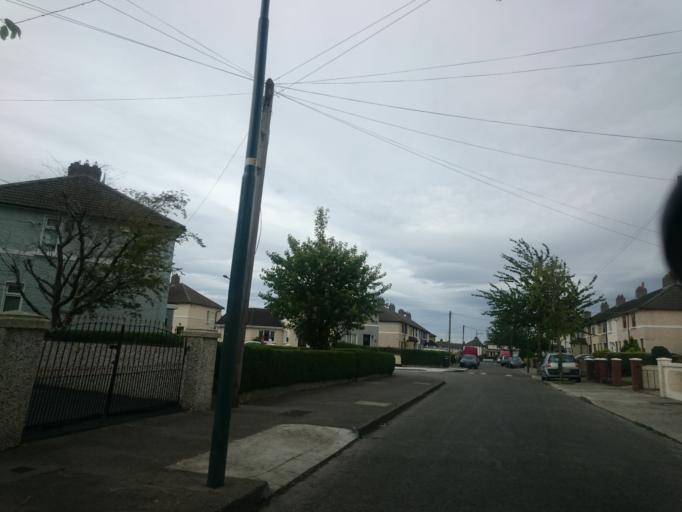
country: IE
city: Greenhills
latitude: 53.3262
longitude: -6.3054
